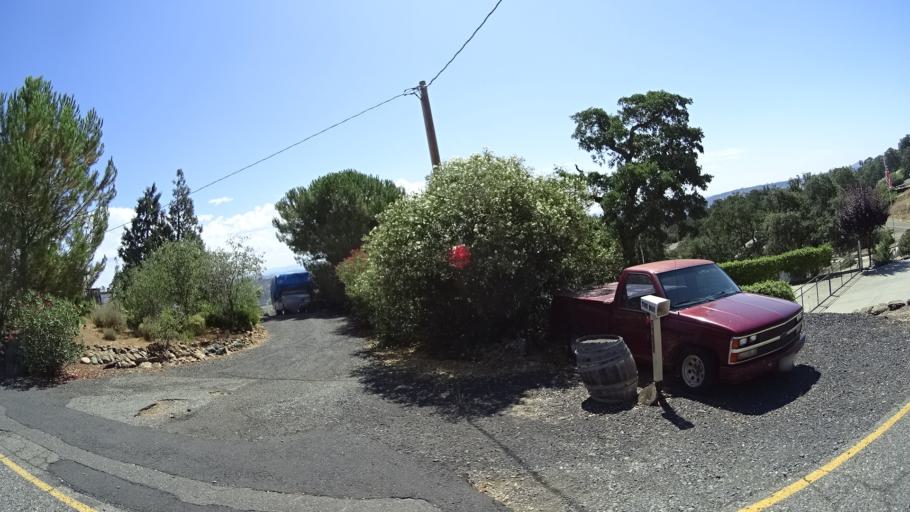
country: US
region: California
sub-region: Calaveras County
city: Copperopolis
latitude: 37.9274
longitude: -120.6303
